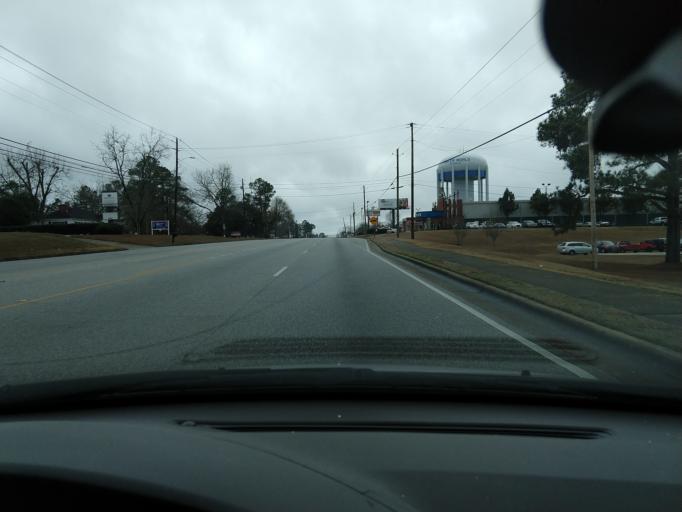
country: US
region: Alabama
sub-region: Houston County
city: Dothan
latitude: 31.2374
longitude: -85.4346
